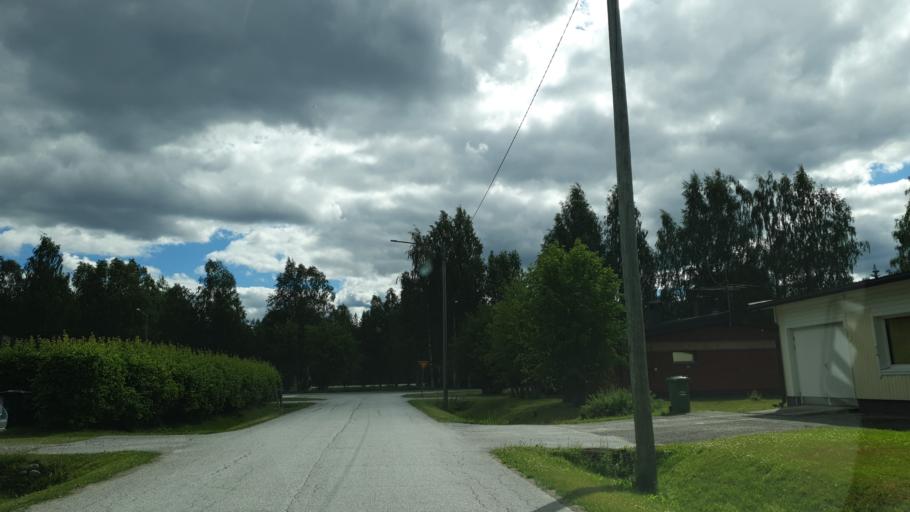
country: FI
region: Kainuu
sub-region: Kehys-Kainuu
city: Kuhmo
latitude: 64.1123
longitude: 29.4875
